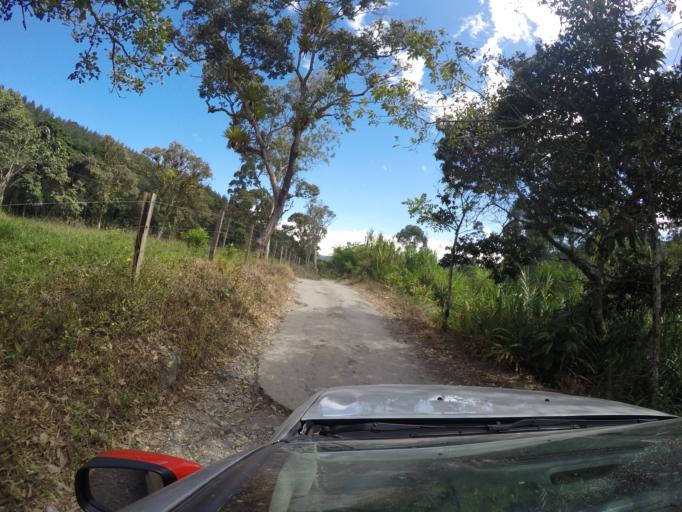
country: CO
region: Quindio
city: Salento
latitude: 4.6331
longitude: -75.5898
